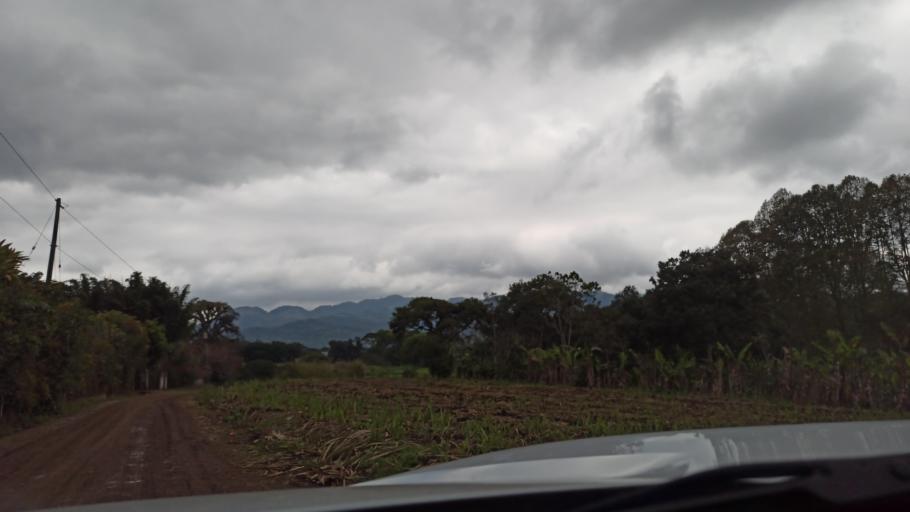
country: MX
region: Veracruz
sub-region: Chocaman
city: San Jose Neria
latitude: 18.9843
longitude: -97.0077
